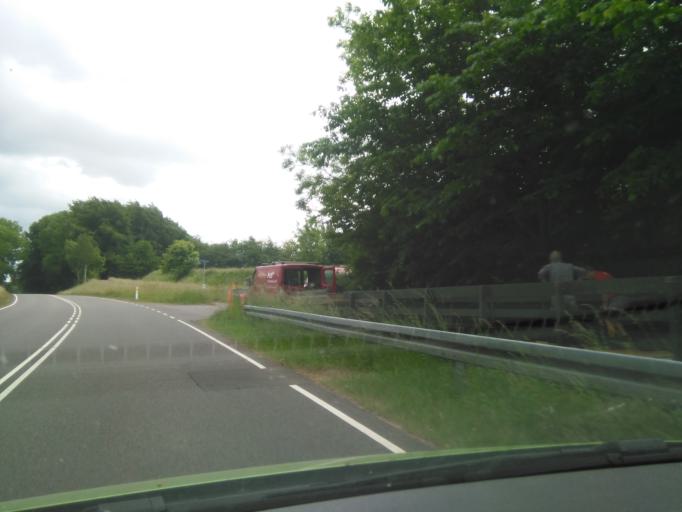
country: DK
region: Capital Region
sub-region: Bornholm Kommune
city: Akirkeby
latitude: 55.2299
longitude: 14.8786
